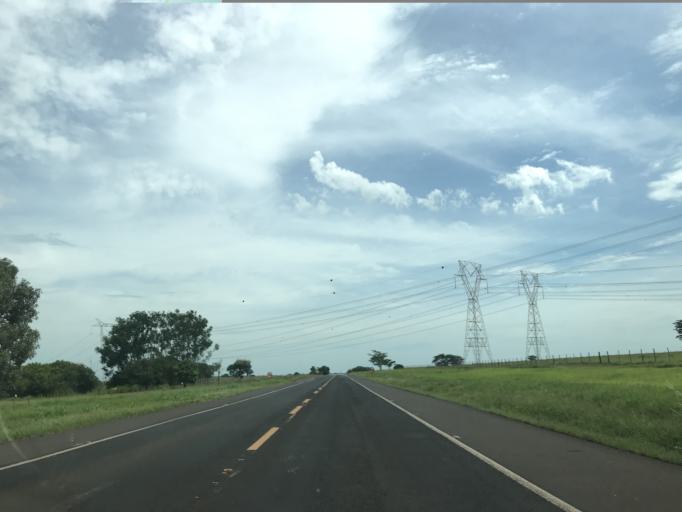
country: BR
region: Sao Paulo
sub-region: Nova Granada
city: Nova Granada
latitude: -20.3383
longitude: -49.2145
